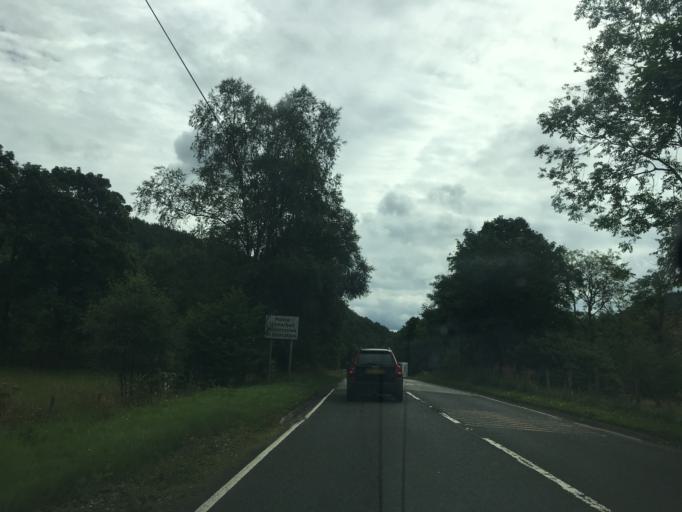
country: GB
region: Scotland
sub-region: Stirling
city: Callander
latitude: 56.2592
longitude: -4.2849
